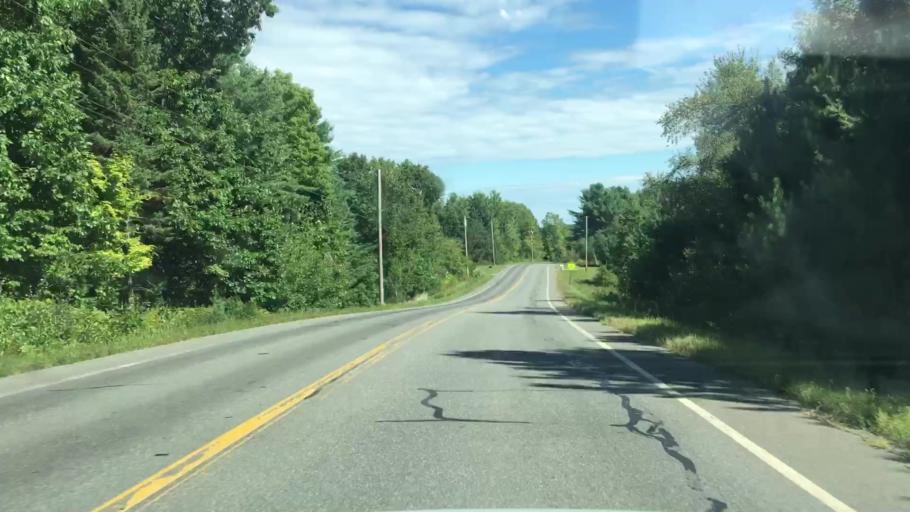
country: US
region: Maine
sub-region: Penobscot County
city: Garland
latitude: 45.0863
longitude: -69.2255
